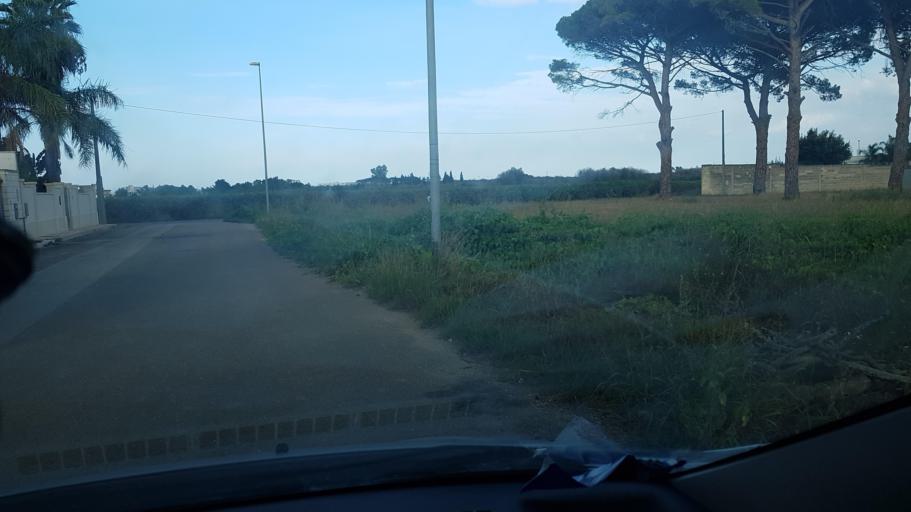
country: IT
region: Apulia
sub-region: Provincia di Brindisi
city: Cellino San Marco
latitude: 40.4693
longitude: 17.9742
